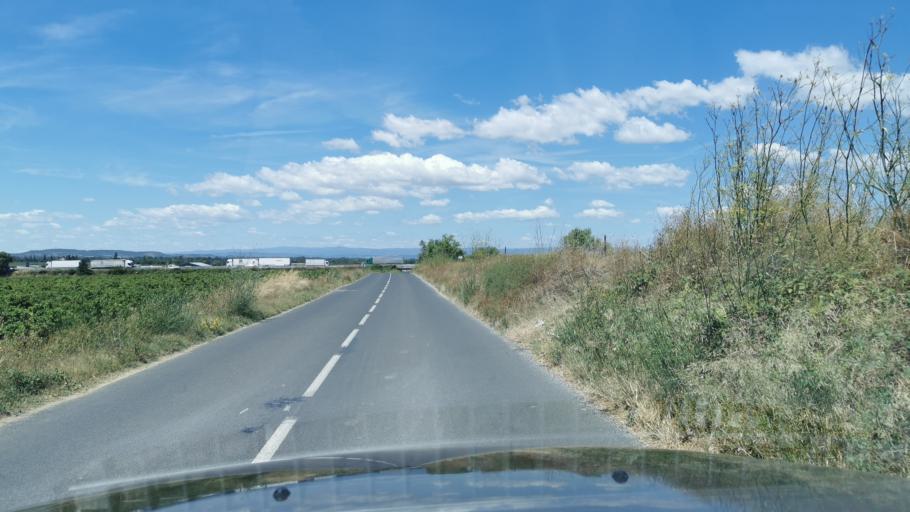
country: FR
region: Languedoc-Roussillon
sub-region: Departement de l'Aude
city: Vinassan
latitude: 43.1939
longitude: 3.0769
